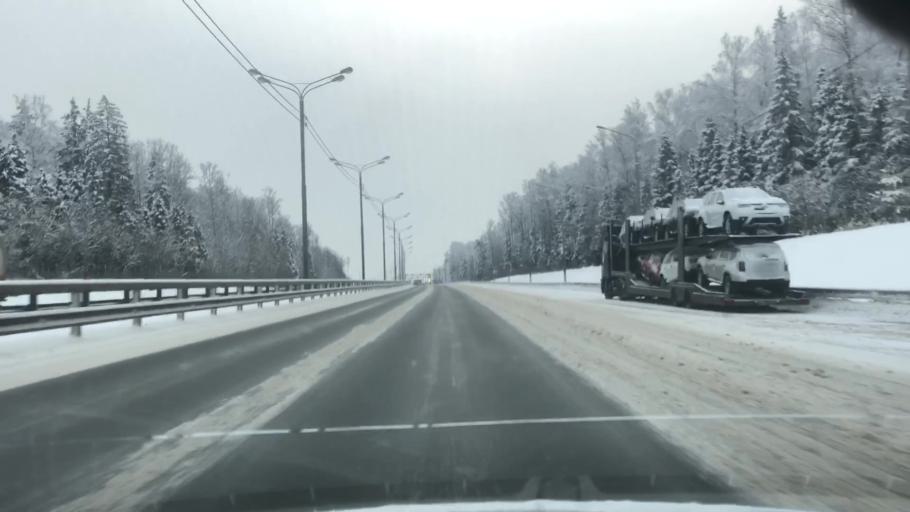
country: RU
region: Moskovskaya
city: Mikhnevo
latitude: 55.1781
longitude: 37.9082
